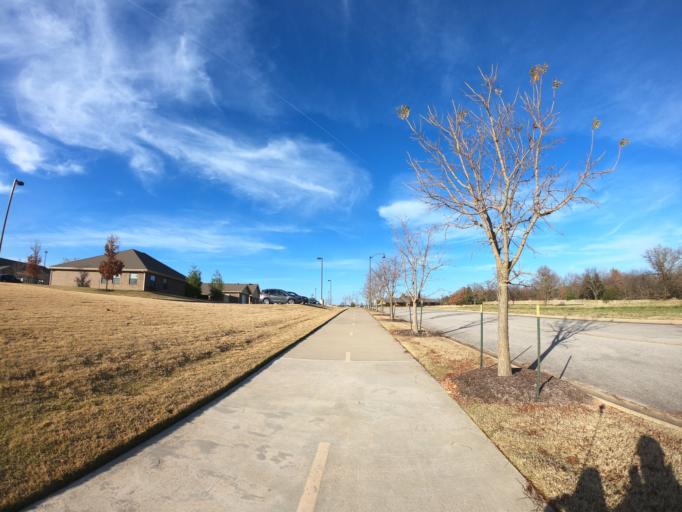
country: US
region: Arkansas
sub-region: Benton County
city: Bentonville
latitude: 36.3252
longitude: -94.1762
